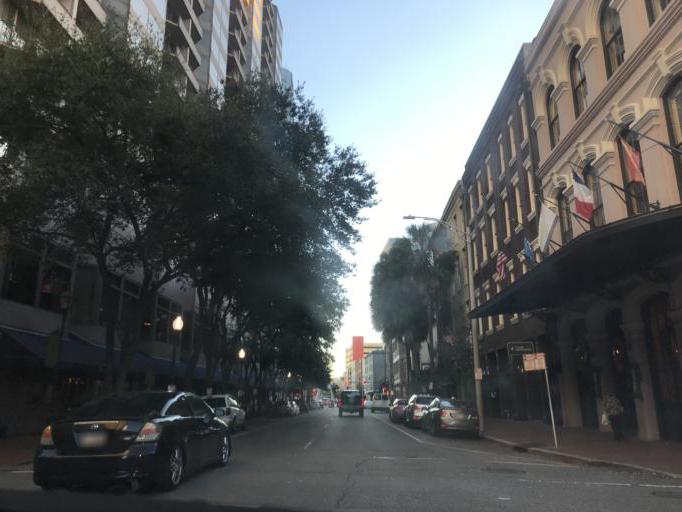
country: US
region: Louisiana
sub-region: Orleans Parish
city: New Orleans
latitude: 29.9501
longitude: -90.0665
